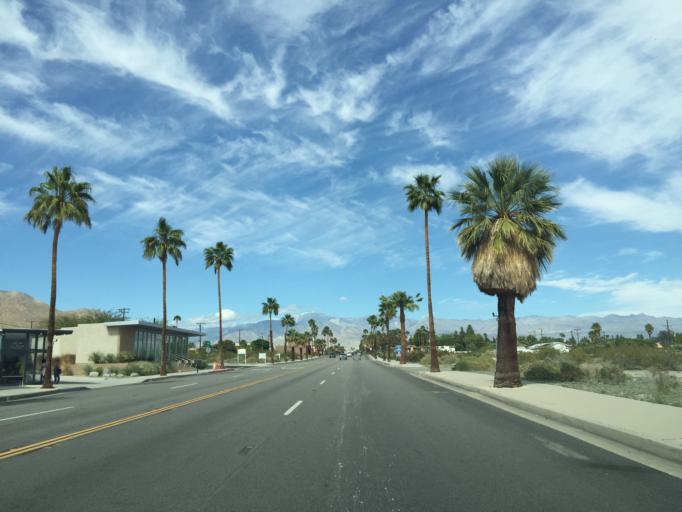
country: US
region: California
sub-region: Riverside County
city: Palm Springs
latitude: 33.8536
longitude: -116.5528
